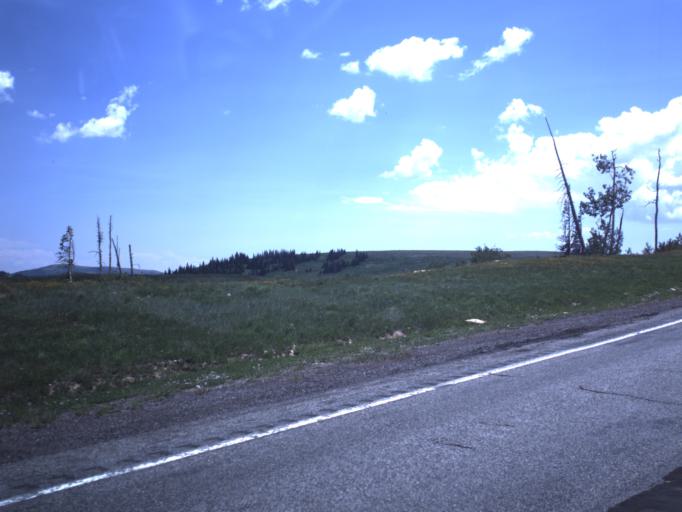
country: US
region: Utah
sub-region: Sanpete County
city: Fairview
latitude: 39.6231
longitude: -111.3157
